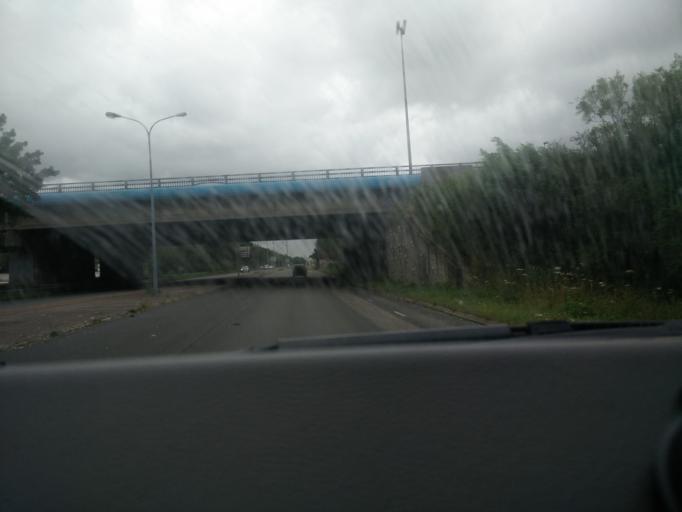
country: FR
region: Nord-Pas-de-Calais
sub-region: Departement du Nord
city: Coudekerque-Branche
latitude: 51.0136
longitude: 2.3787
